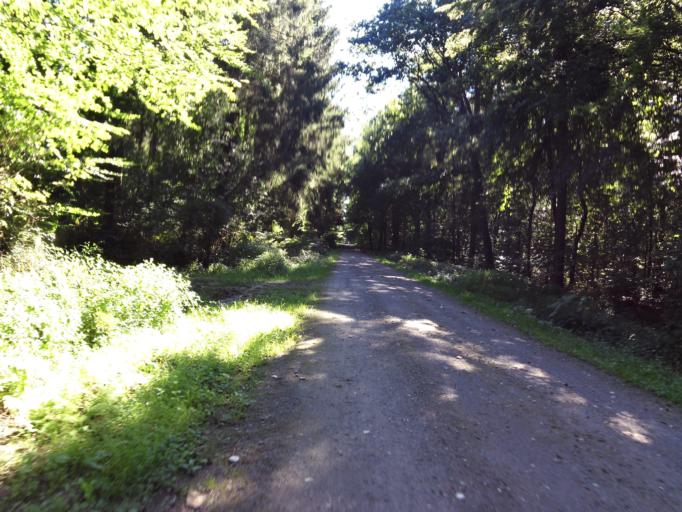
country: NL
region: Gelderland
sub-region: Gemeente Groesbeek
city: De Horst
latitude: 51.7469
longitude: 5.9872
